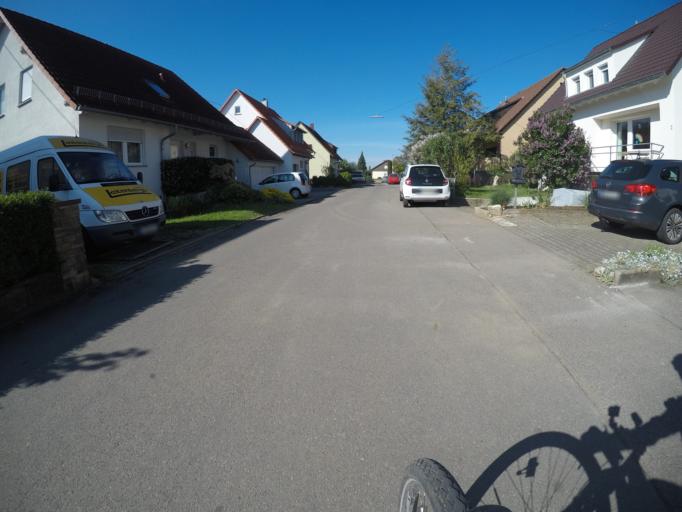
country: DE
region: Baden-Wuerttemberg
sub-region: Regierungsbezirk Stuttgart
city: Altenriet
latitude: 48.5964
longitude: 9.1961
